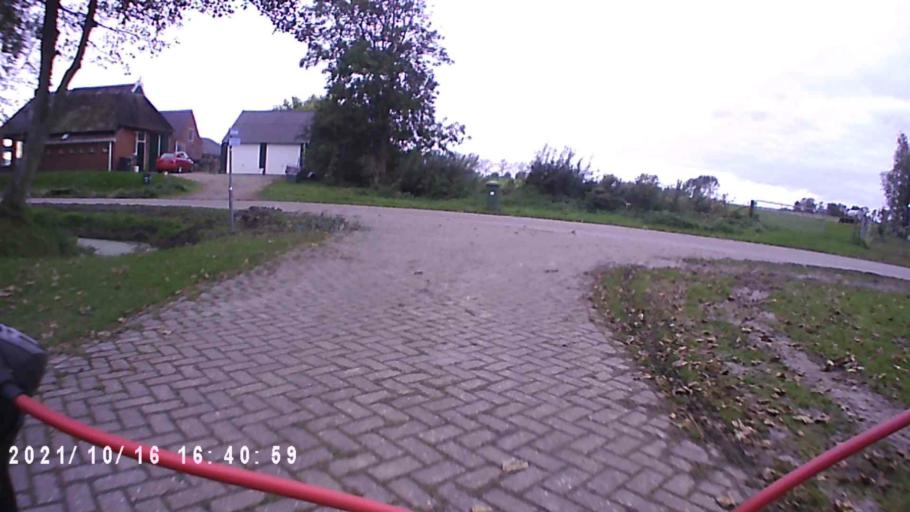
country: NL
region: Friesland
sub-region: Gemeente Dongeradeel
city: Anjum
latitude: 53.3783
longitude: 6.1446
